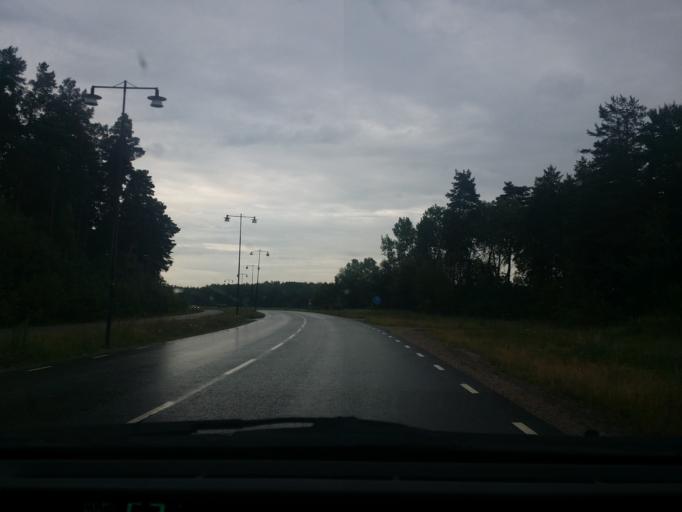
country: SE
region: Vaestmanland
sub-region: Arboga Kommun
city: Arboga
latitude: 59.4093
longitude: 15.8344
